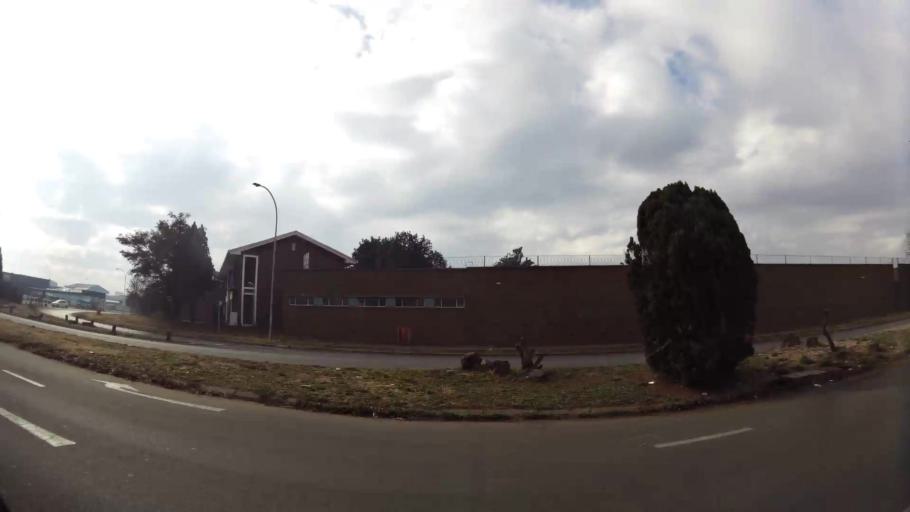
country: ZA
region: Gauteng
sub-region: Sedibeng District Municipality
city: Vanderbijlpark
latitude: -26.6986
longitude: 27.8323
